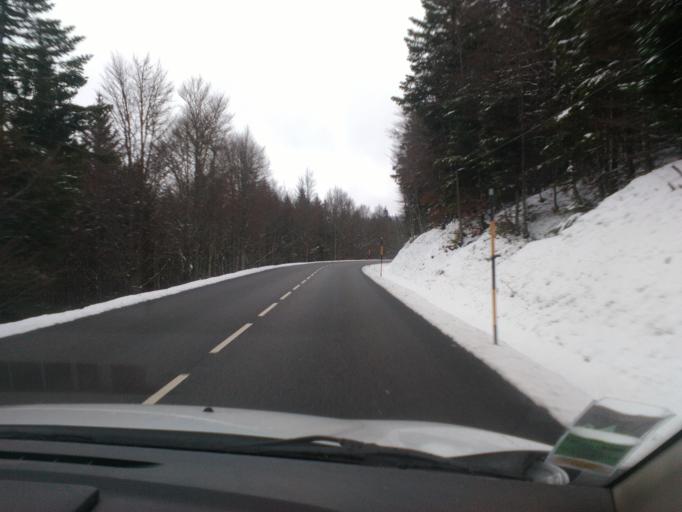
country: FR
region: Alsace
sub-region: Departement du Haut-Rhin
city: Metzeral
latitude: 48.0610
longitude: 7.0137
